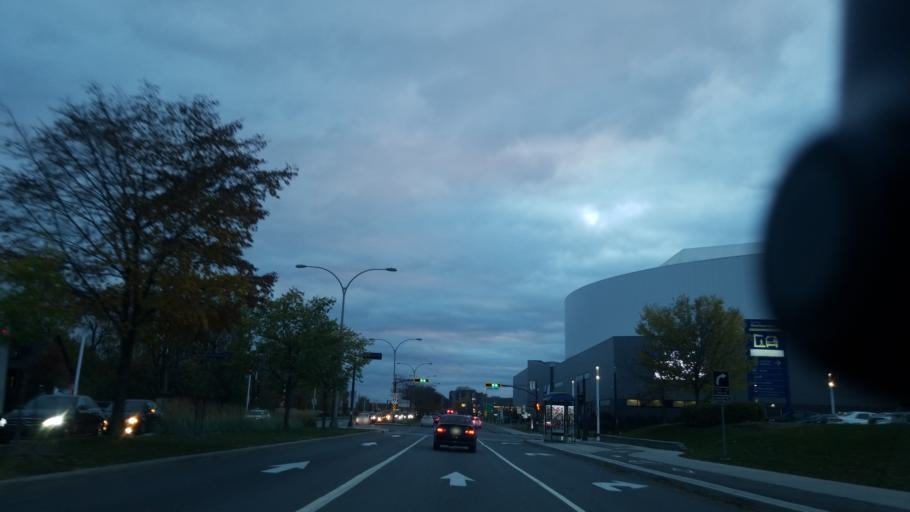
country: CA
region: Quebec
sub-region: Laval
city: Laval
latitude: 45.5563
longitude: -73.7191
